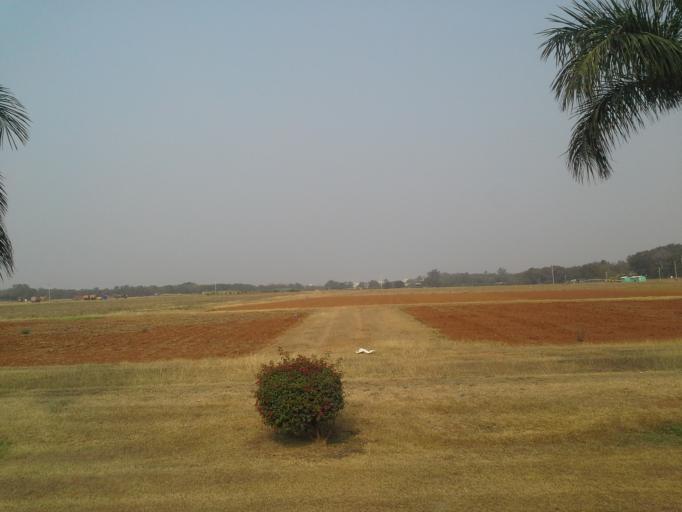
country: IN
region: Telangana
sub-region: Medak
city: Patancheru
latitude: 17.5158
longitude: 78.2770
